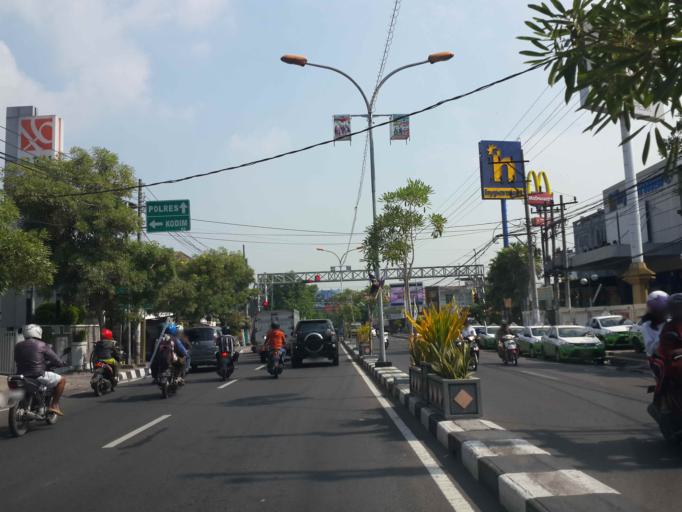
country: ID
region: East Java
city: Gresik
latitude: -7.1721
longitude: 112.6532
